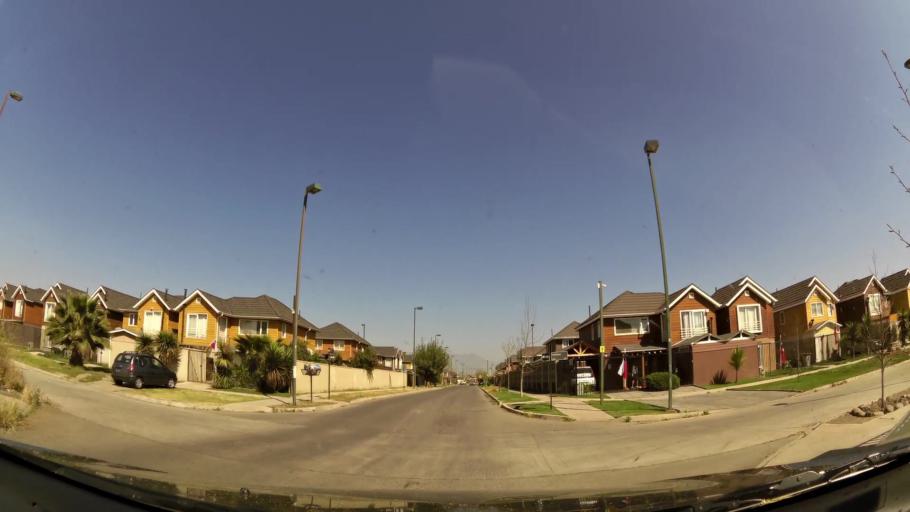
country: CL
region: Santiago Metropolitan
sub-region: Provincia de Chacabuco
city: Chicureo Abajo
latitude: -33.3259
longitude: -70.7436
